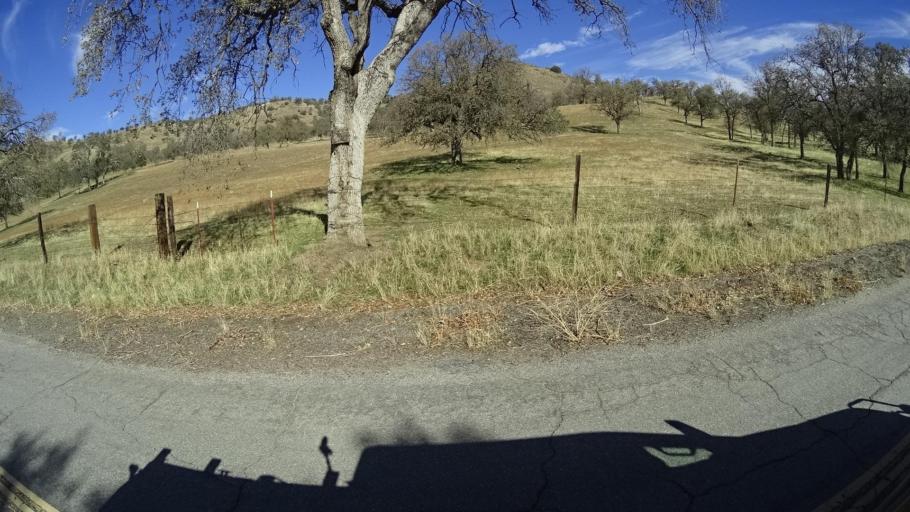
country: US
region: California
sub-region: Kern County
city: Alta Sierra
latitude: 35.6298
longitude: -118.7899
